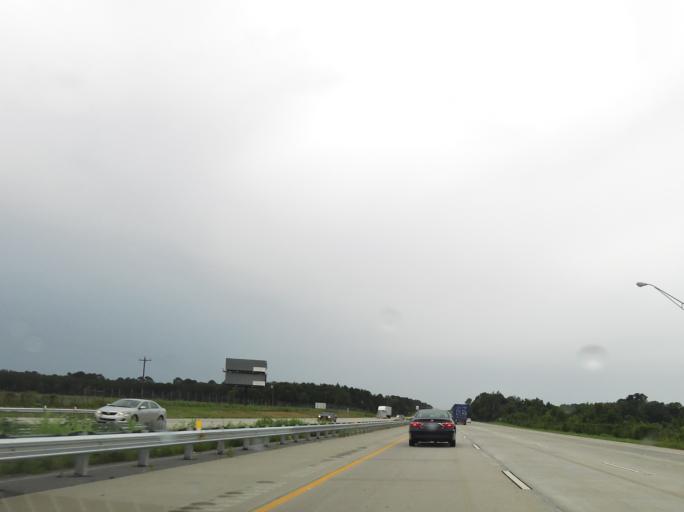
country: US
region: Georgia
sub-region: Dooly County
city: Vienna
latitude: 32.0833
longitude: -83.7635
